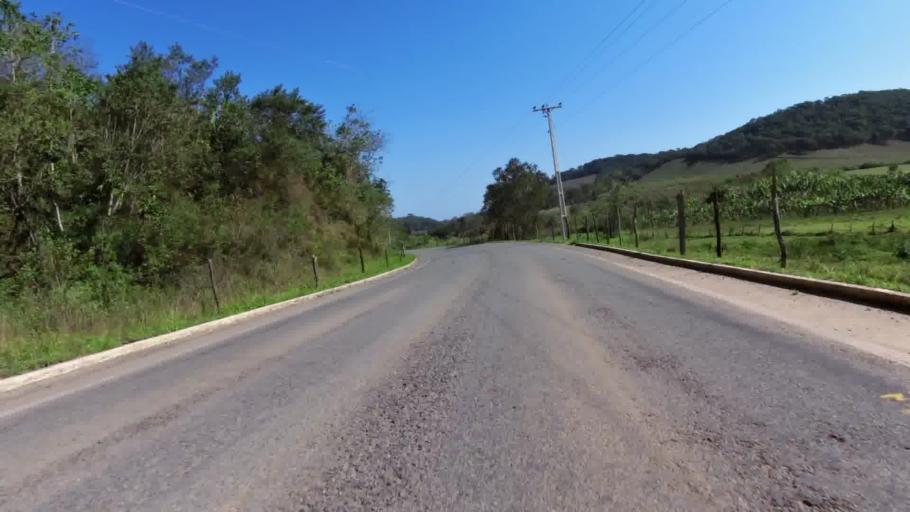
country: BR
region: Espirito Santo
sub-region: Alfredo Chaves
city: Alfredo Chaves
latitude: -20.5448
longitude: -40.7874
